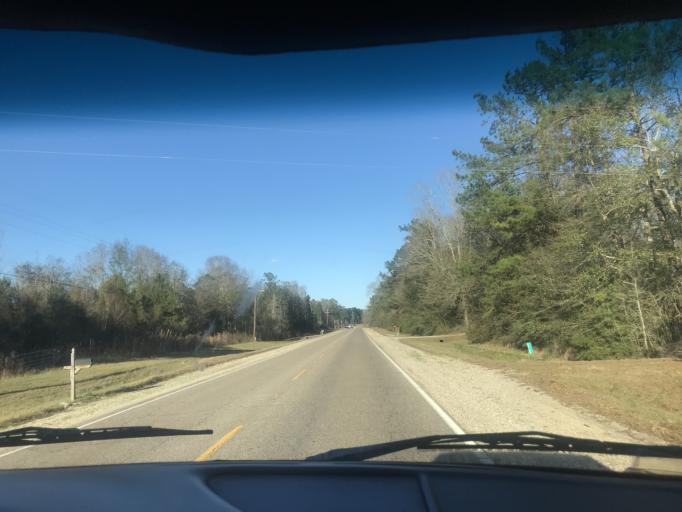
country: US
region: Louisiana
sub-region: Washington Parish
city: Franklinton
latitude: 30.6715
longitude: -90.2006
